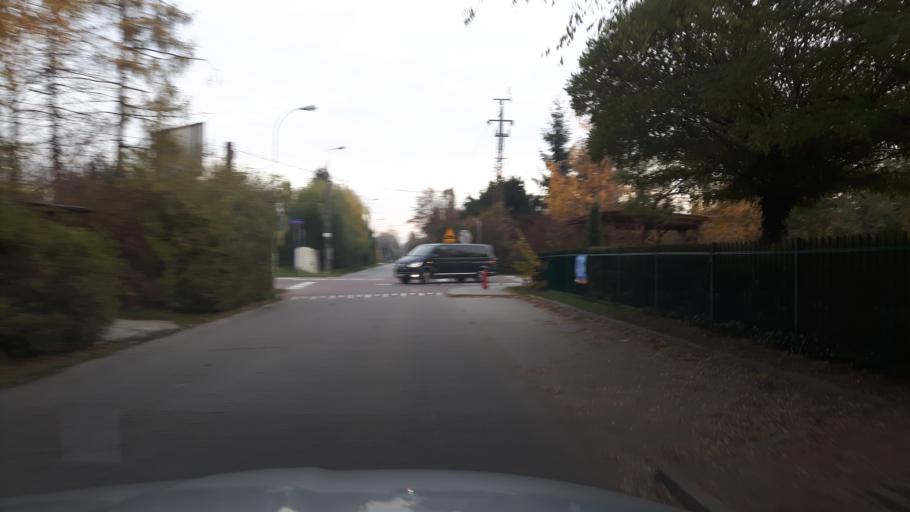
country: PL
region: Masovian Voivodeship
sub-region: Warszawa
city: Wilanow
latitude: 52.1691
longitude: 21.1157
